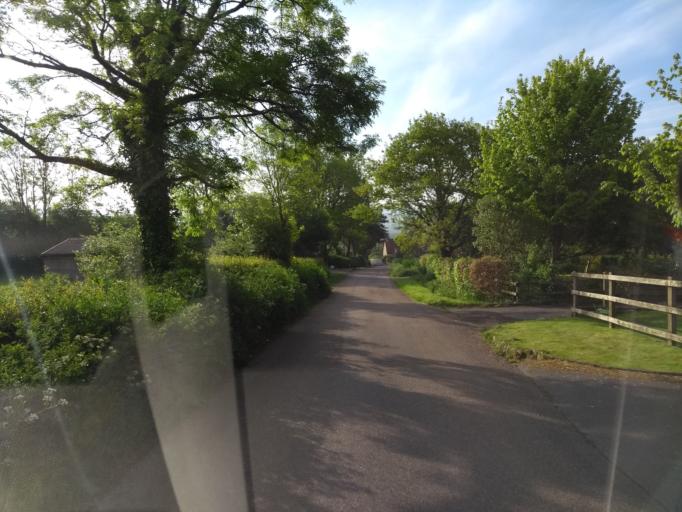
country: GB
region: England
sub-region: Somerset
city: Chard
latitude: 50.8235
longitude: -2.9652
